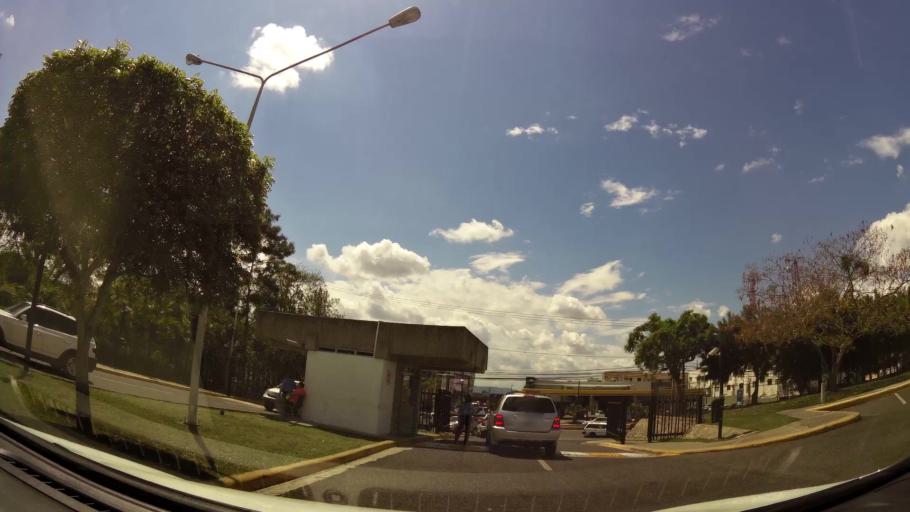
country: DO
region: Santiago
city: Santiago de los Caballeros
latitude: 19.4424
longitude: -70.6867
